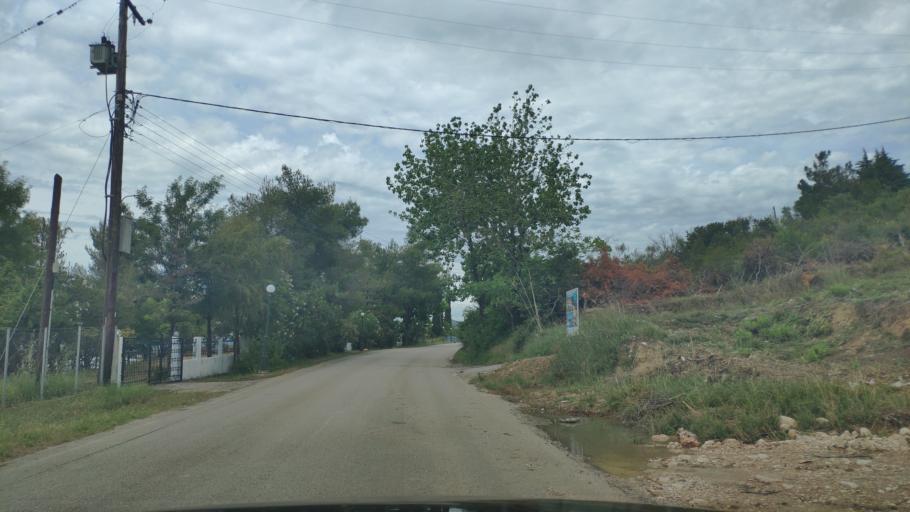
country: GR
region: West Greece
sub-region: Nomos Aitolias kai Akarnanias
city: Palairos
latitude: 38.7758
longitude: 20.8822
